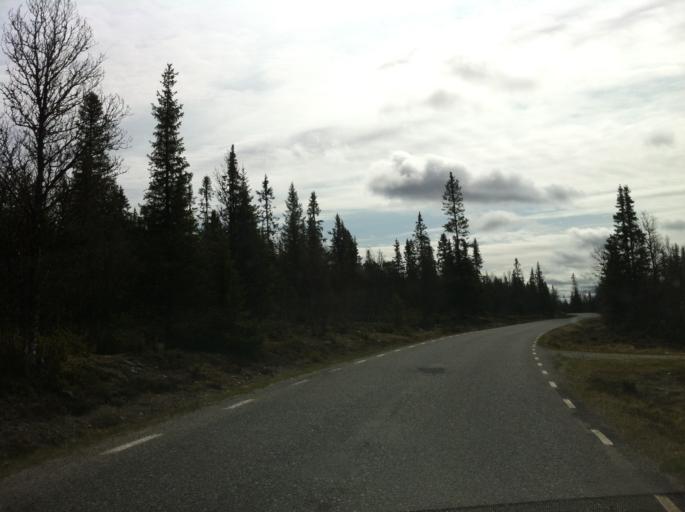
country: NO
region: Hedmark
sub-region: Engerdal
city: Engerdal
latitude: 62.3078
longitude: 12.8062
